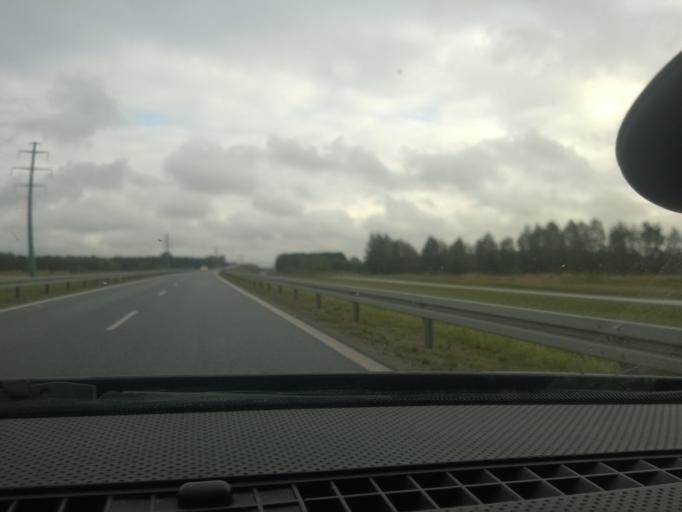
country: PL
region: Lodz Voivodeship
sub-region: Powiat sieradzki
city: Sieradz
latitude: 51.5785
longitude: 18.6812
